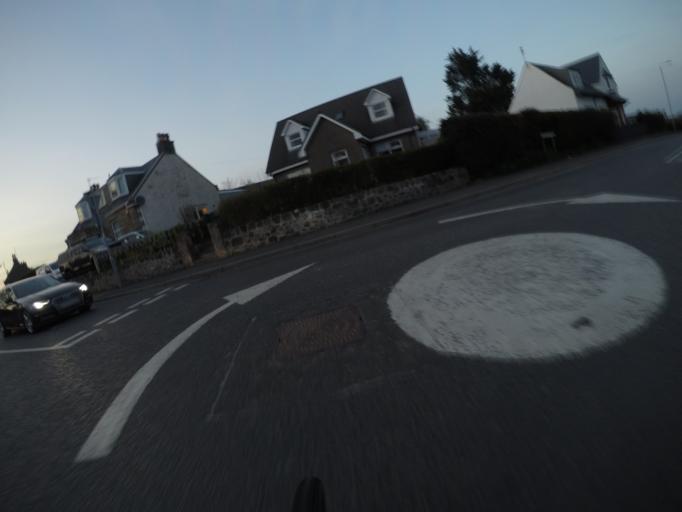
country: GB
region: Scotland
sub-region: South Ayrshire
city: Dundonald
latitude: 55.5741
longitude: -4.5918
